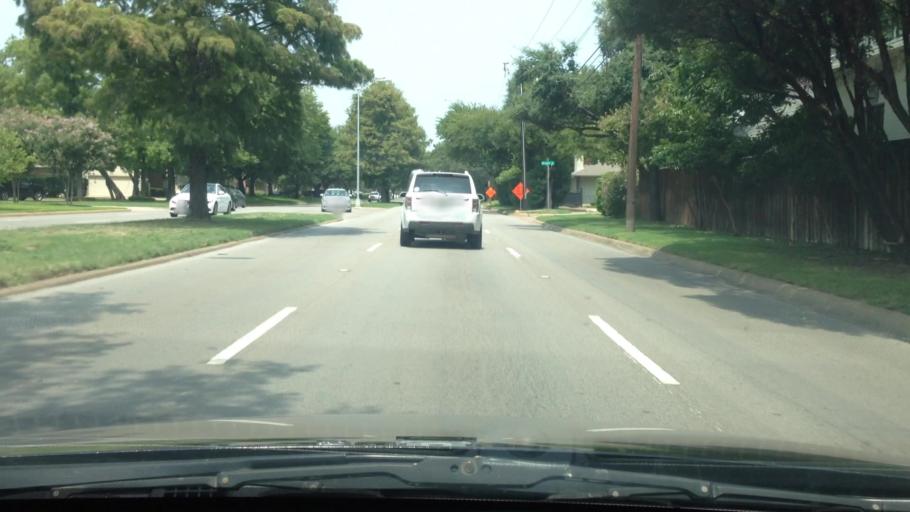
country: US
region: Texas
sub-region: Dallas County
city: University Park
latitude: 32.8420
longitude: -96.8214
